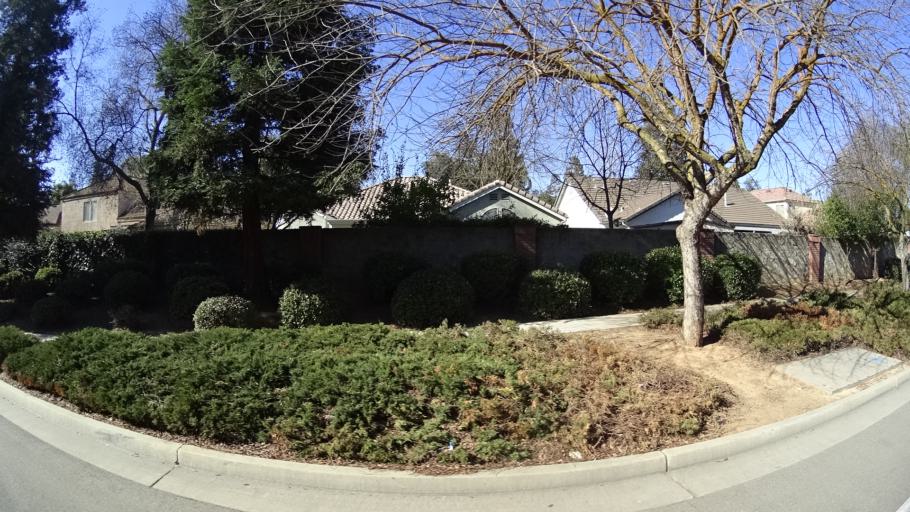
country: US
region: California
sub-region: Fresno County
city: Fresno
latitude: 36.8278
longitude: -119.8547
